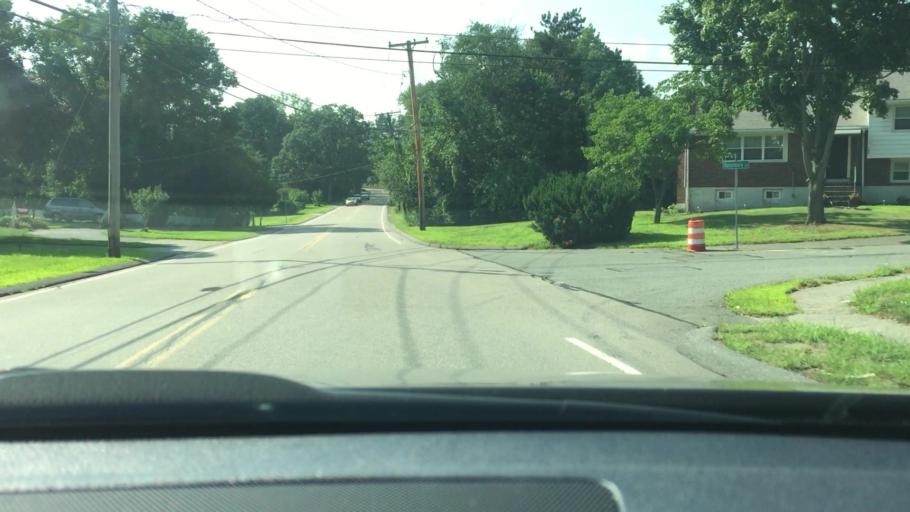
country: US
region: Massachusetts
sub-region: Norfolk County
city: Dedham
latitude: 42.2692
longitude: -71.1865
